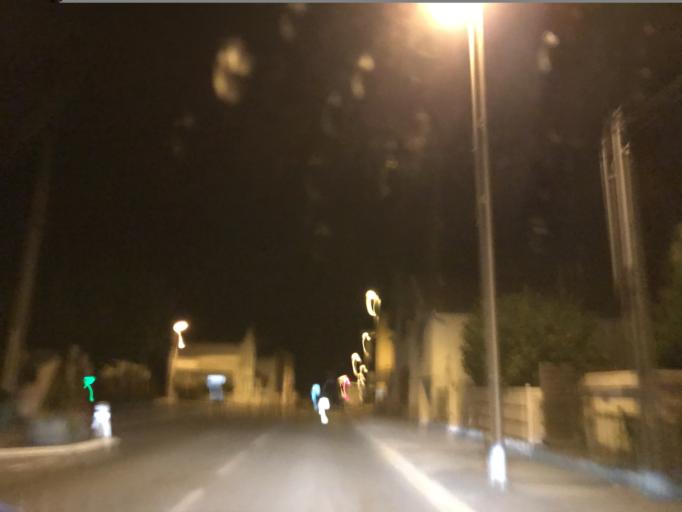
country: FR
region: Auvergne
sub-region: Departement de l'Allier
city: Saint-Yorre
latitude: 46.0675
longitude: 3.4647
